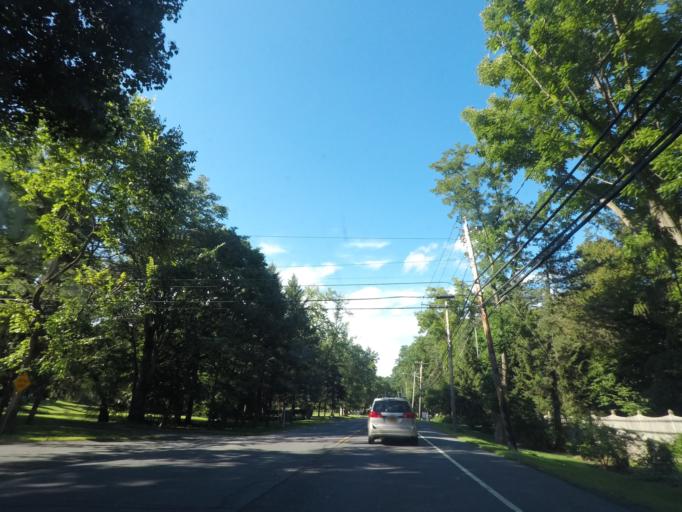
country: US
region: New York
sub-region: Albany County
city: West Albany
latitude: 42.6913
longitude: -73.7529
